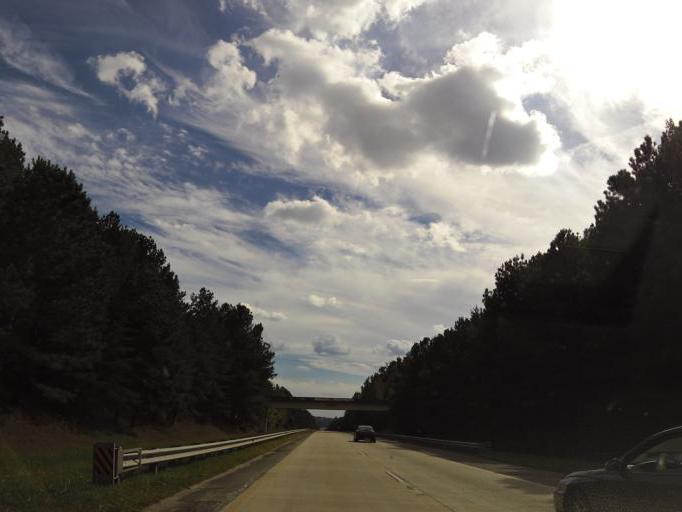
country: US
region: Georgia
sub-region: Cherokee County
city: Ball Ground
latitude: 34.3609
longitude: -84.3916
